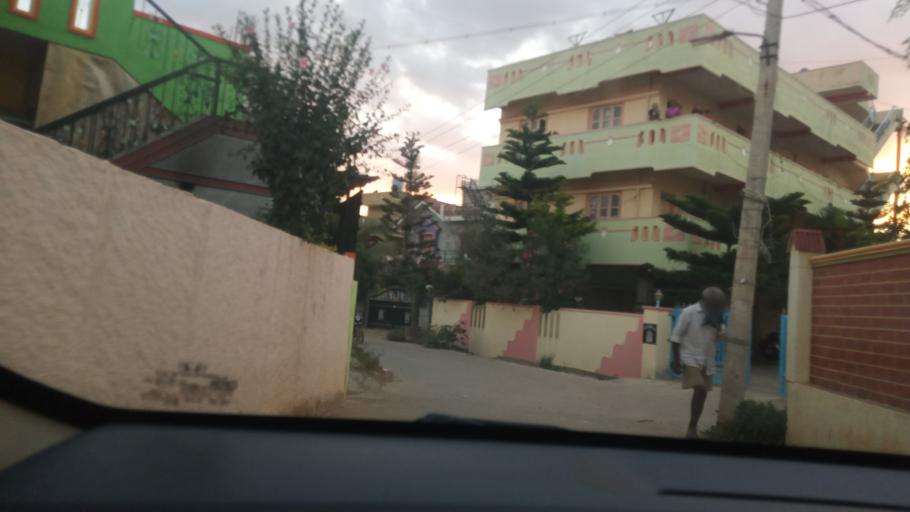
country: IN
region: Karnataka
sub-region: Bangalore Rural
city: Hoskote
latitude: 12.9770
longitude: 77.8013
